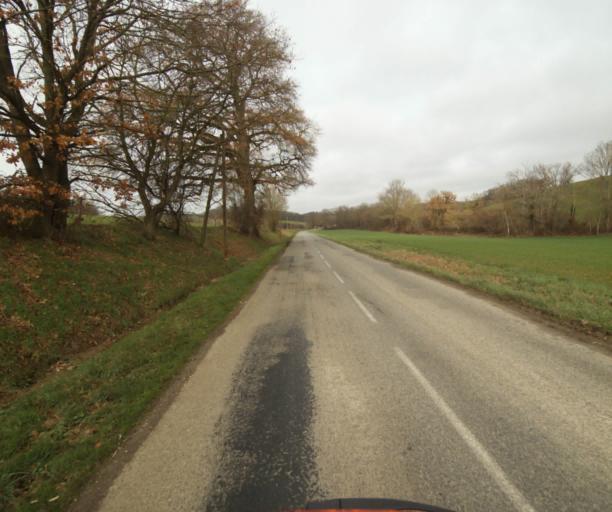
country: FR
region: Midi-Pyrenees
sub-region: Departement de l'Ariege
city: Pamiers
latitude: 43.1400
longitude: 1.5339
